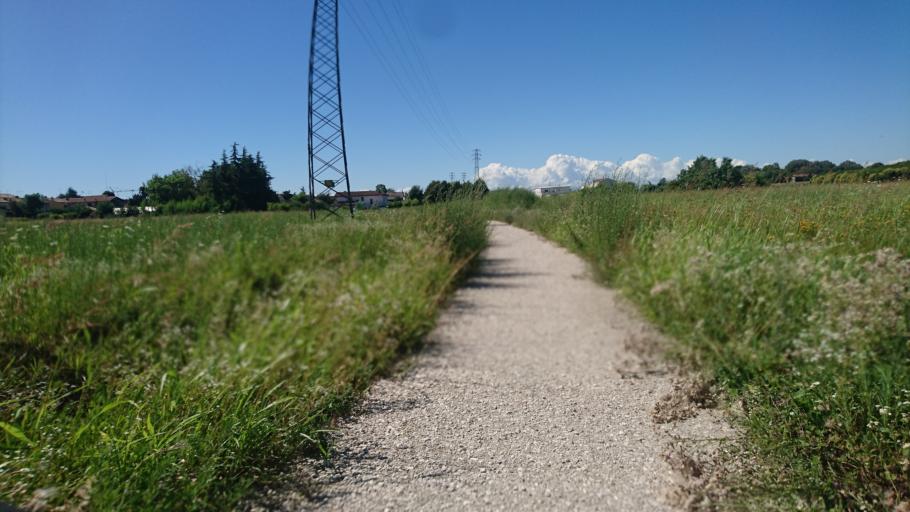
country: IT
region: Veneto
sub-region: Provincia di Padova
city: Piove di Sacco-Piovega
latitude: 45.2894
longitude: 12.0266
